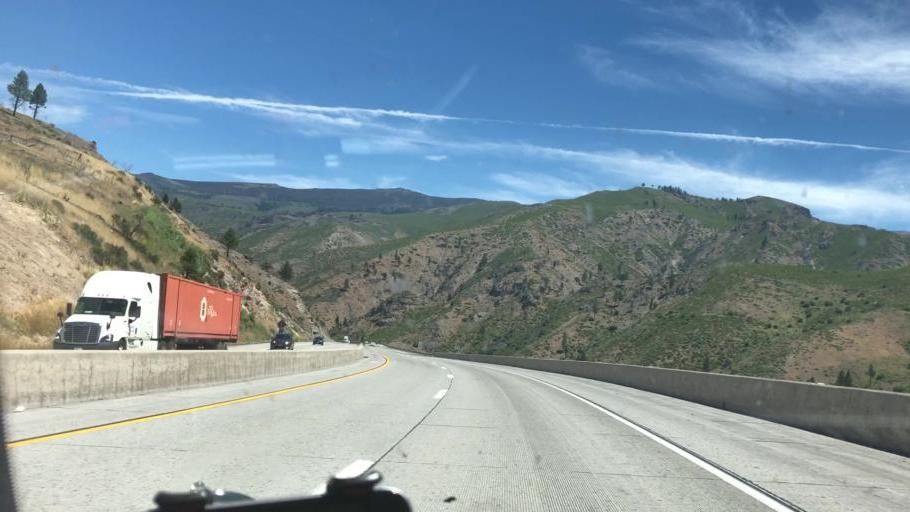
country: US
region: California
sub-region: Placer County
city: Tahoe Vista
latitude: 39.3695
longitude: -120.0462
